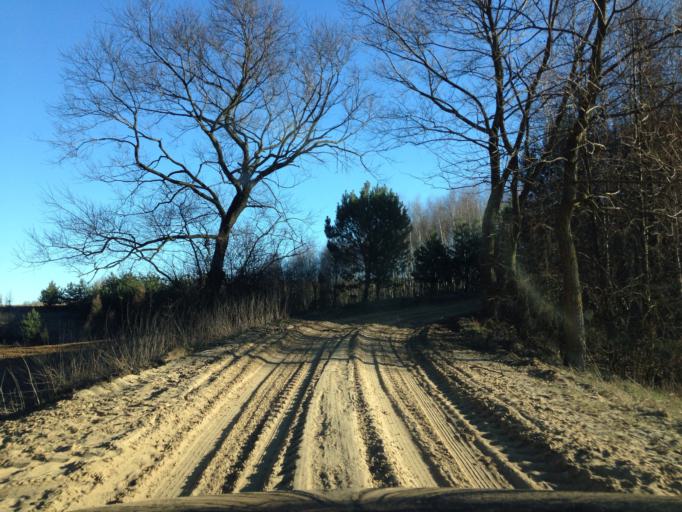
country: PL
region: Kujawsko-Pomorskie
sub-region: Powiat brodnicki
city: Brzozie
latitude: 53.3099
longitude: 19.6577
